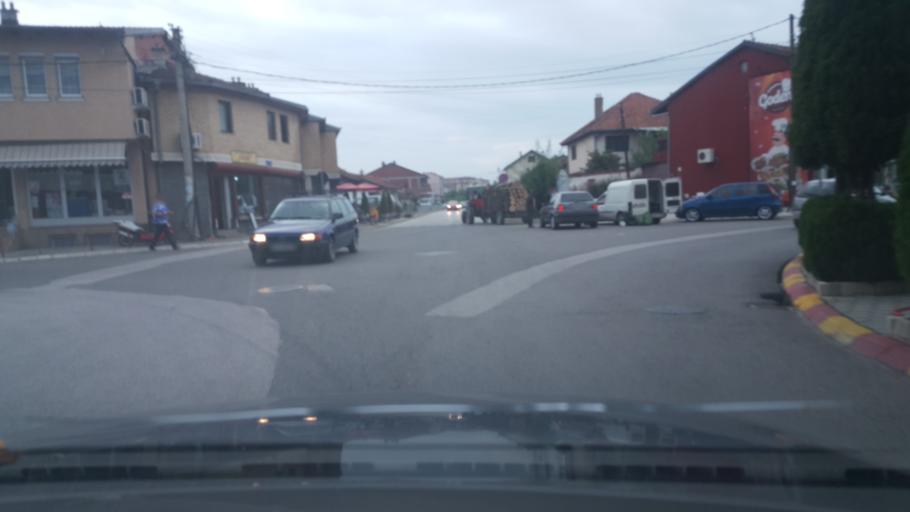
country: XK
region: Gjakova
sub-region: Komuna e Gjakoves
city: Gjakove
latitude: 42.3884
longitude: 20.4317
